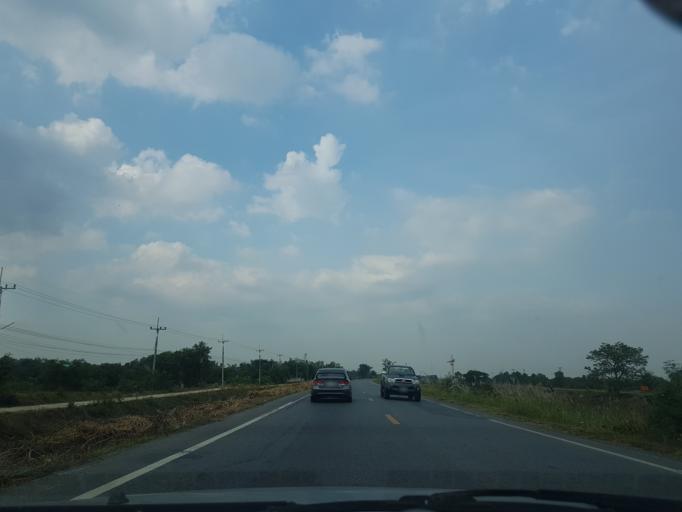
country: TH
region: Phra Nakhon Si Ayutthaya
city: Phachi
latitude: 14.4923
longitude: 100.7363
